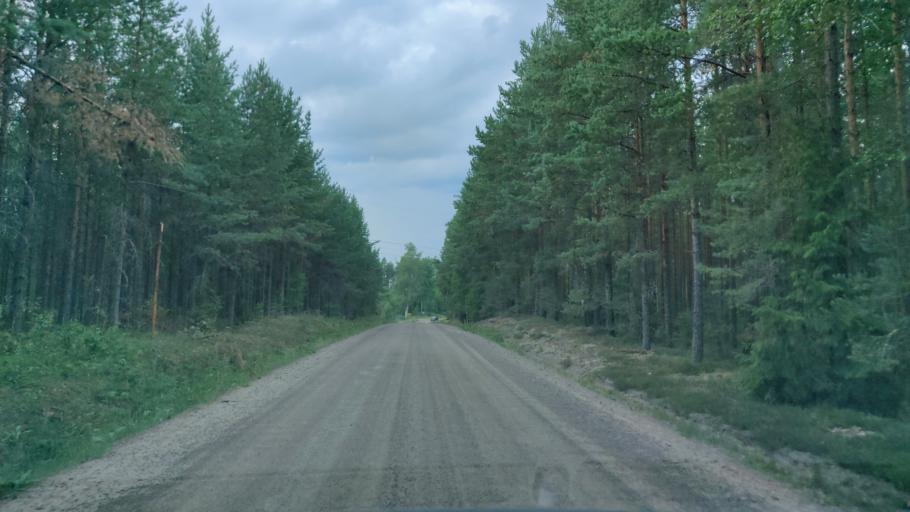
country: SE
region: Vaermland
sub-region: Munkfors Kommun
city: Munkfors
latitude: 59.9583
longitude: 13.4953
